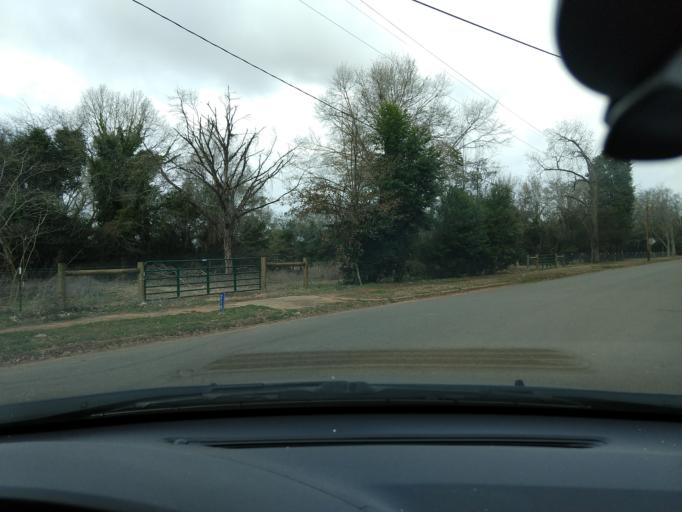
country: US
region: Georgia
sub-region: Calhoun County
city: Edison
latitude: 31.5168
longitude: -84.8649
